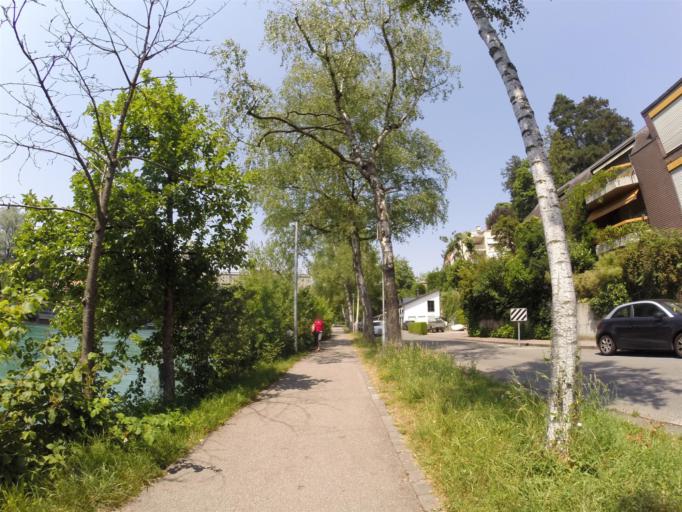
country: CH
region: Bern
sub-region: Bern-Mittelland District
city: Bern
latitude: 46.9434
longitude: 7.4458
